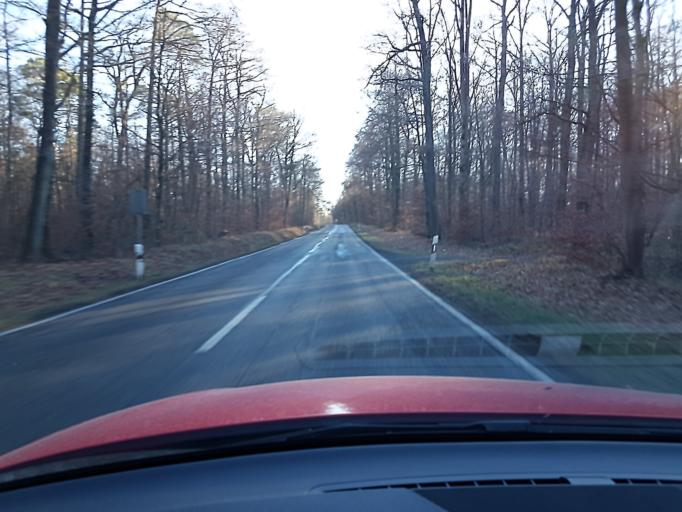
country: DE
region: Baden-Wuerttemberg
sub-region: Regierungsbezirk Stuttgart
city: Freudental
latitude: 49.0175
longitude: 9.0663
